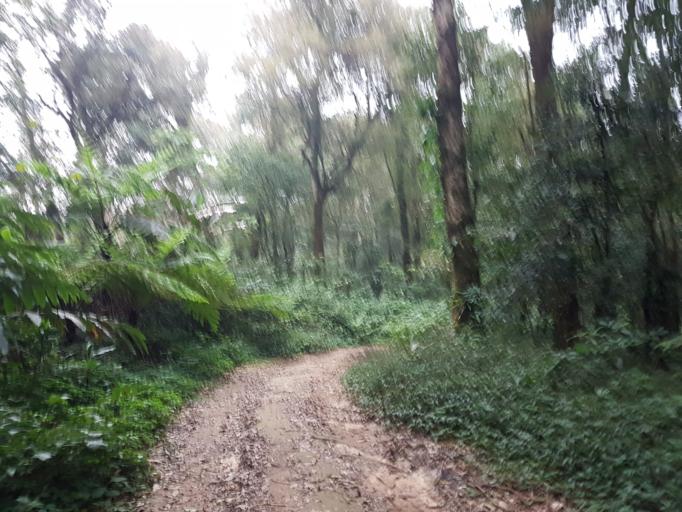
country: TH
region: Phetchabun
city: Lom Kao
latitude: 16.8929
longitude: 101.0942
